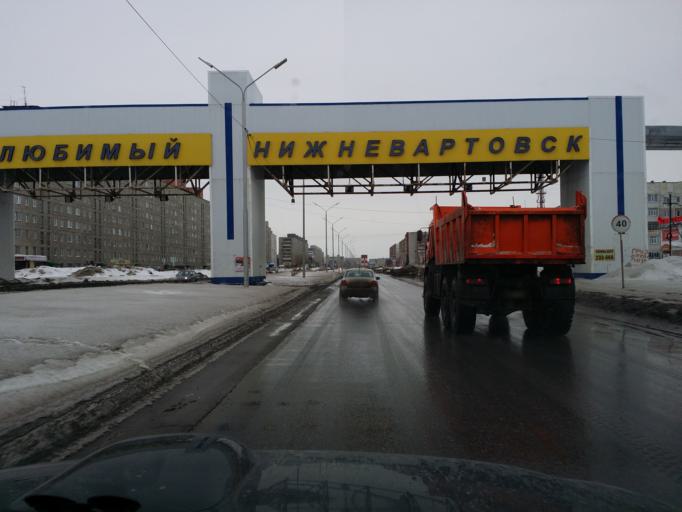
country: RU
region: Khanty-Mansiyskiy Avtonomnyy Okrug
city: Nizhnevartovsk
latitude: 60.9409
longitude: 76.6182
